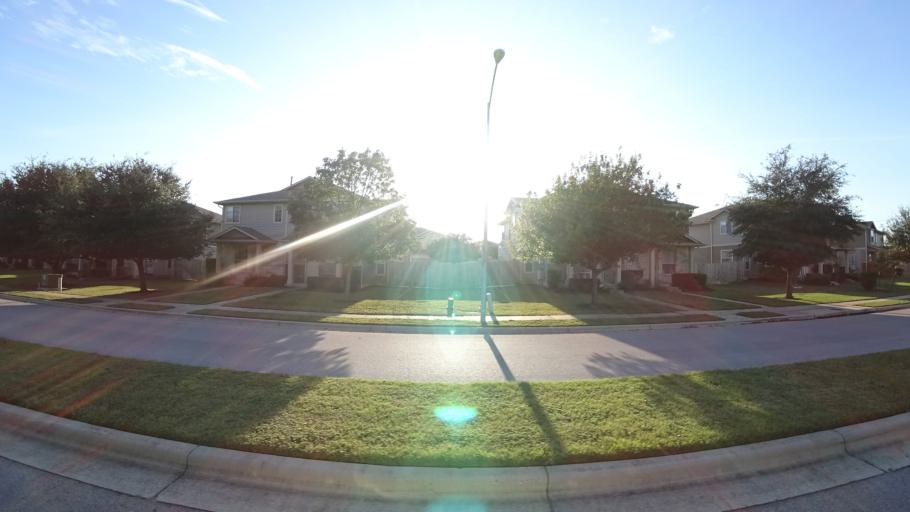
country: US
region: Texas
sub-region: Travis County
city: Pflugerville
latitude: 30.4223
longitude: -97.6446
